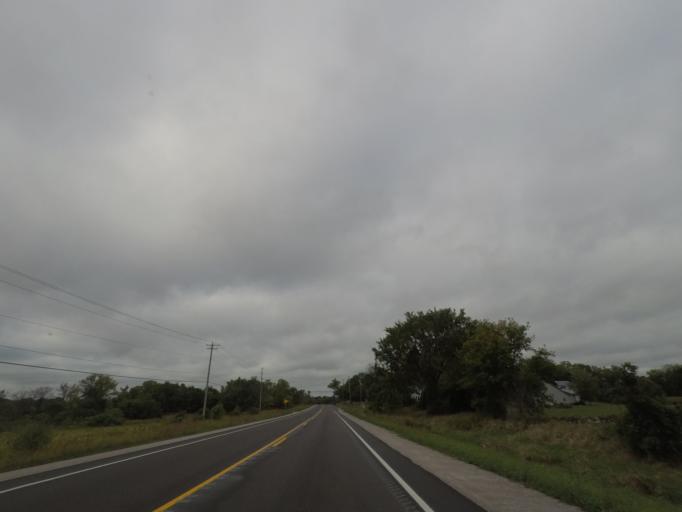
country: US
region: Wisconsin
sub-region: Jefferson County
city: Johnson Creek
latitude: 43.0173
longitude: -88.7366
